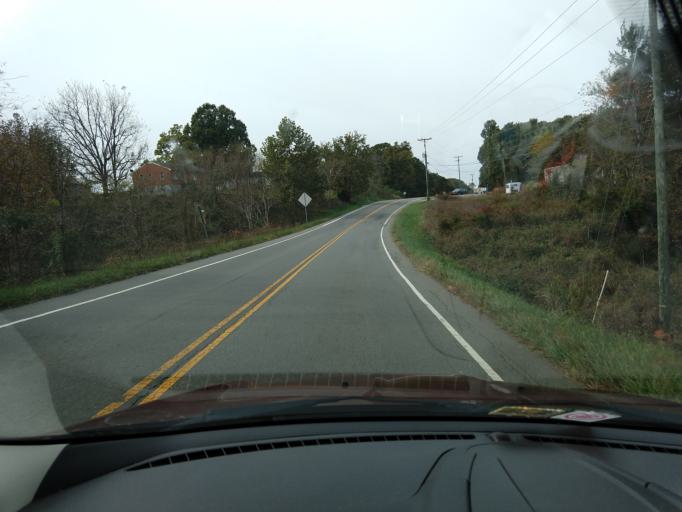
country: US
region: Virginia
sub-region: Franklin County
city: Union Hall
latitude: 36.9935
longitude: -79.7099
